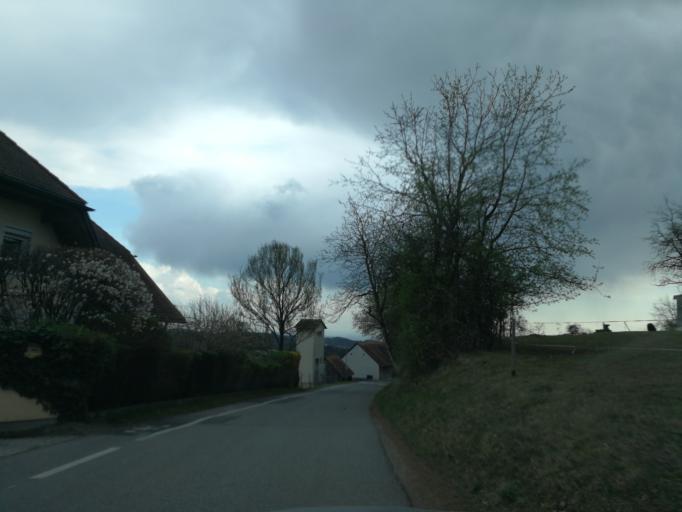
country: AT
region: Styria
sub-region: Politischer Bezirk Graz-Umgebung
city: Hart bei Graz
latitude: 47.0610
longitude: 15.5149
